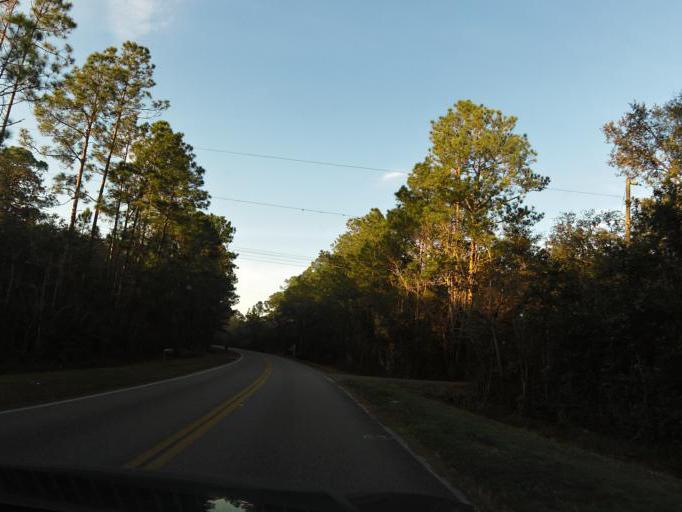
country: US
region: Florida
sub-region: Clay County
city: Green Cove Springs
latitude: 29.8674
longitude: -81.5446
